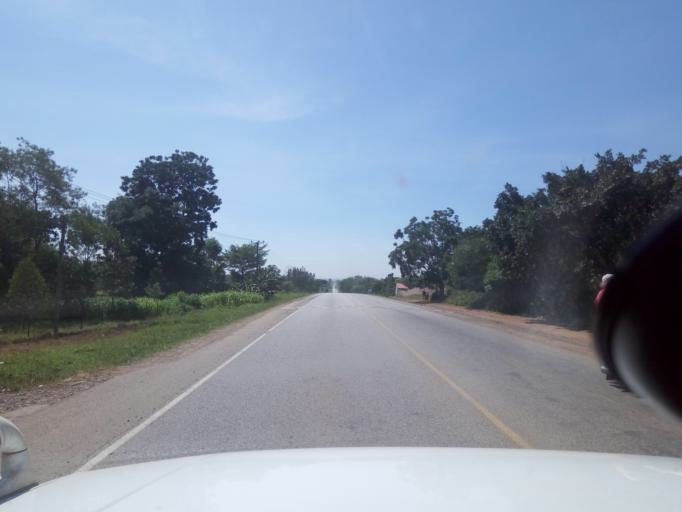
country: UG
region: Eastern Region
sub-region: Tororo District
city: Tororo
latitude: 0.6520
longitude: 34.2192
